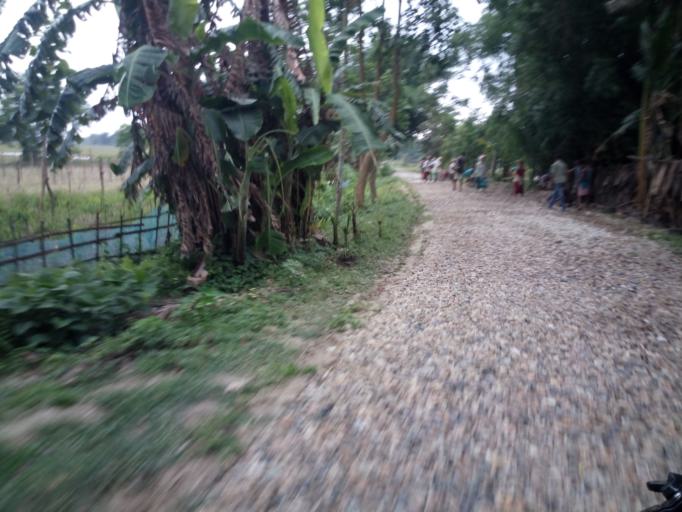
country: IN
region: Assam
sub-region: Darrang
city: Kharupatia
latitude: 26.6512
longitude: 92.2388
